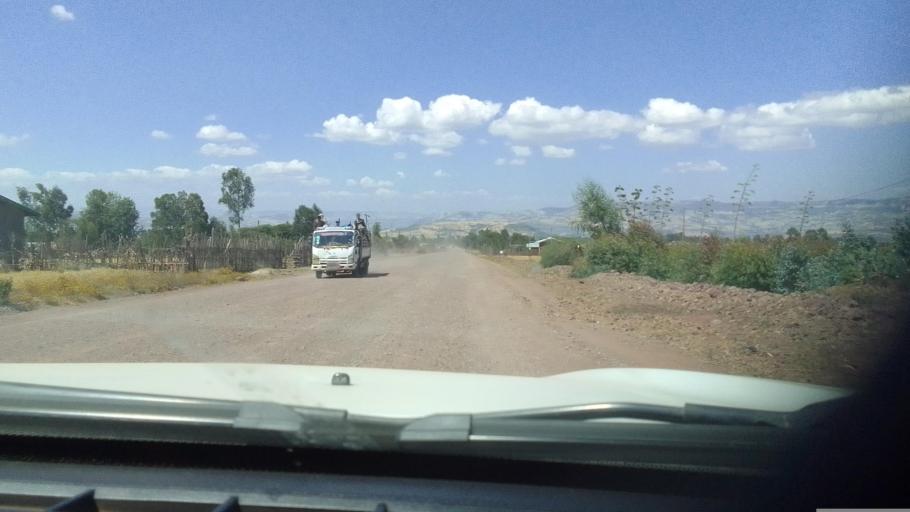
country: ET
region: Oromiya
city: Hagere Hiywet
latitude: 8.9262
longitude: 37.8617
